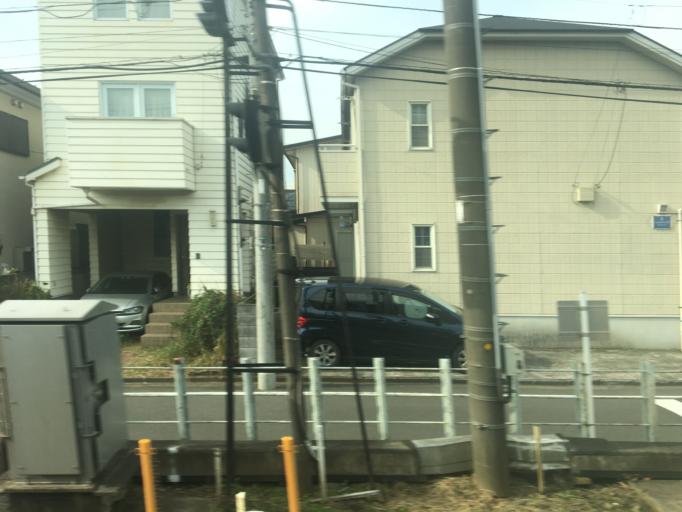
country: JP
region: Saitama
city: Sayama
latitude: 35.8350
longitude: 139.4246
